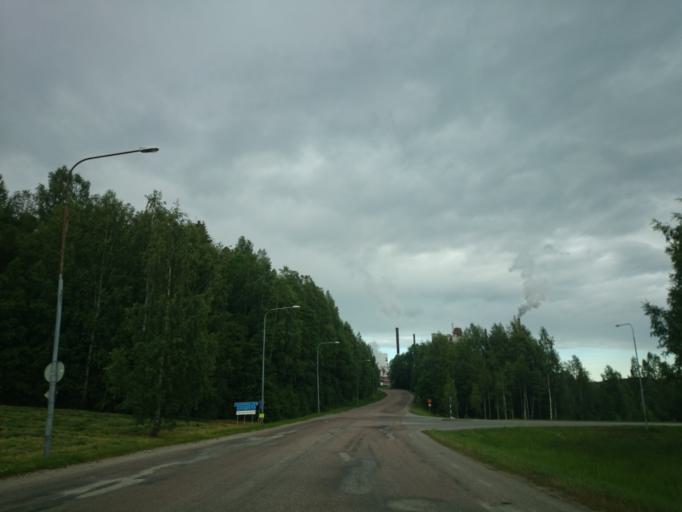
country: SE
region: Vaesternorrland
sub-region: Timra Kommun
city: Timra
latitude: 62.4771
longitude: 17.3160
